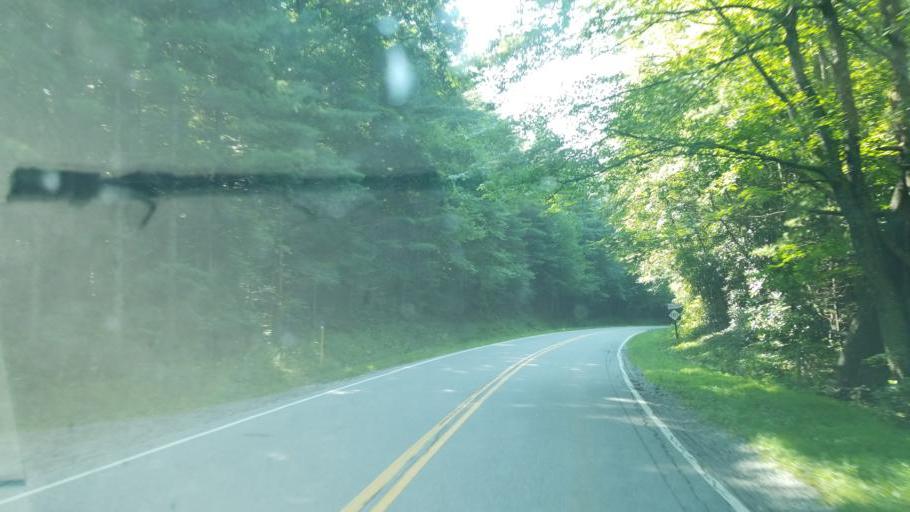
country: US
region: North Carolina
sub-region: Avery County
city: Newland
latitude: 36.0043
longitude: -81.8901
